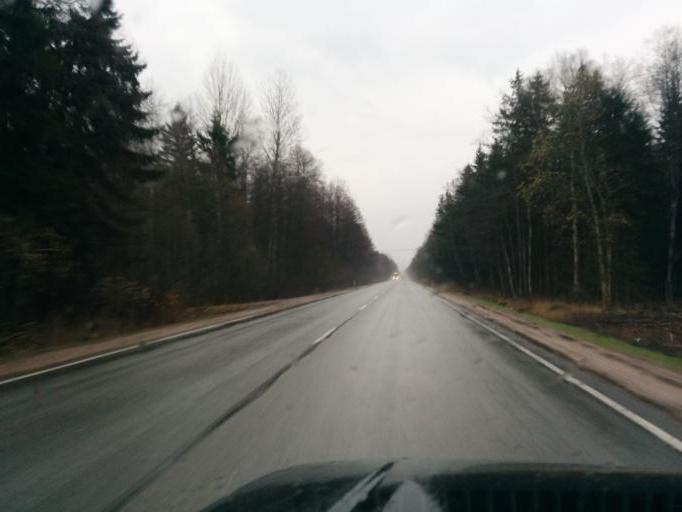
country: LV
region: Kekava
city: Balozi
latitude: 56.8214
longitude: 24.0880
